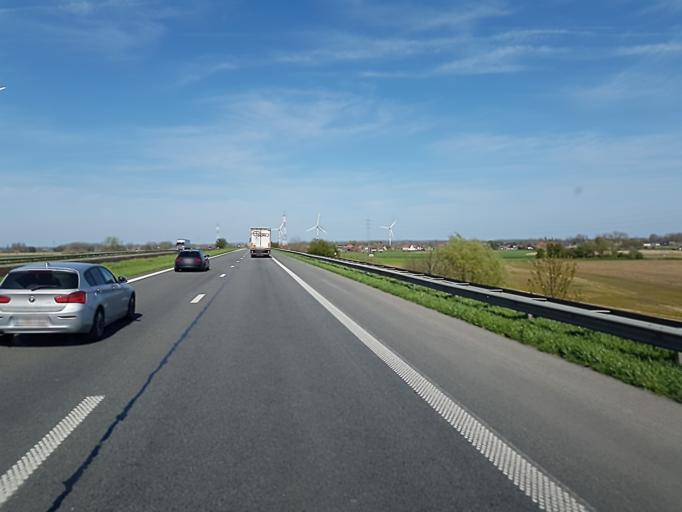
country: BE
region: Wallonia
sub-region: Province du Hainaut
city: Estaimpuis
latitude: 50.6724
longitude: 3.2895
